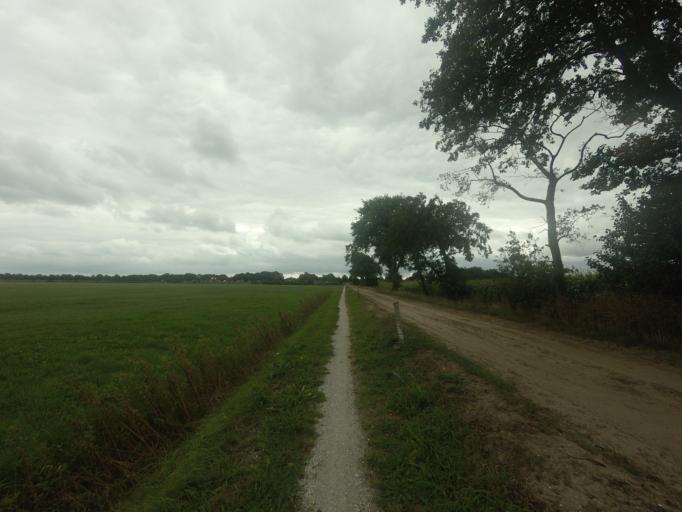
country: NL
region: Friesland
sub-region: Gemeente Weststellingwerf
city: Noordwolde
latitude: 52.9150
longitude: 6.1977
